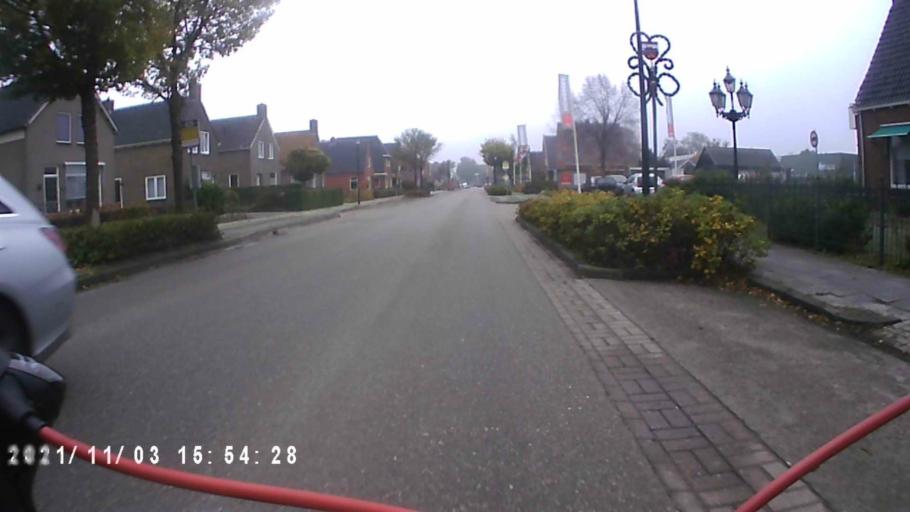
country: NL
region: Groningen
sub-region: Gemeente Leek
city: Leek
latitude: 53.0680
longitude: 6.3318
